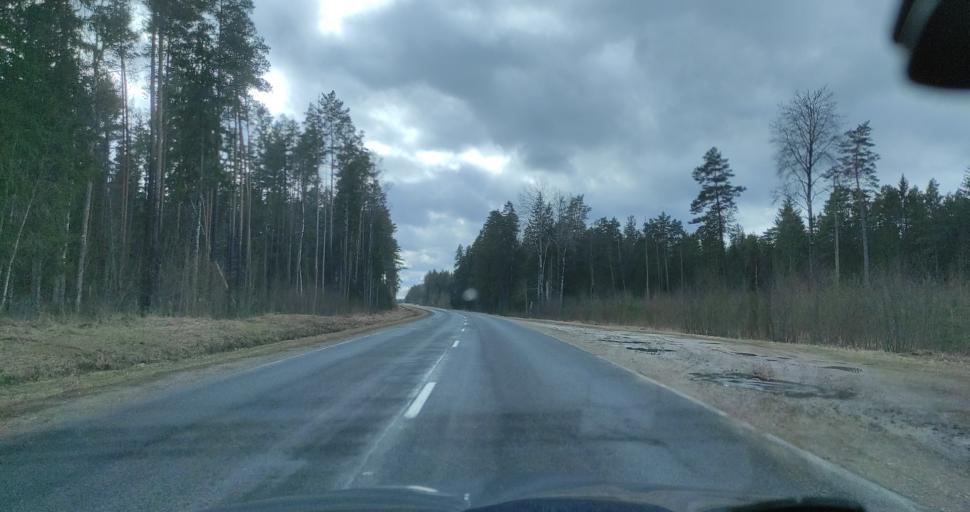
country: LV
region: Talsu Rajons
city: Stende
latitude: 57.1026
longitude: 22.4853
